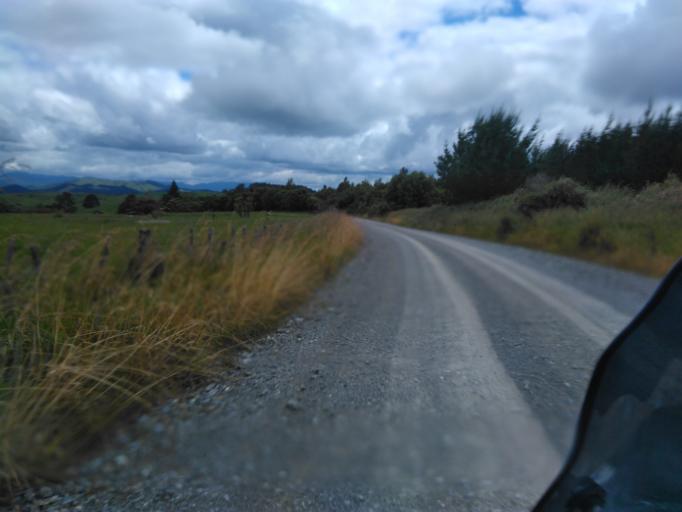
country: NZ
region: Gisborne
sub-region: Gisborne District
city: Gisborne
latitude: -38.1621
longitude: 178.1346
